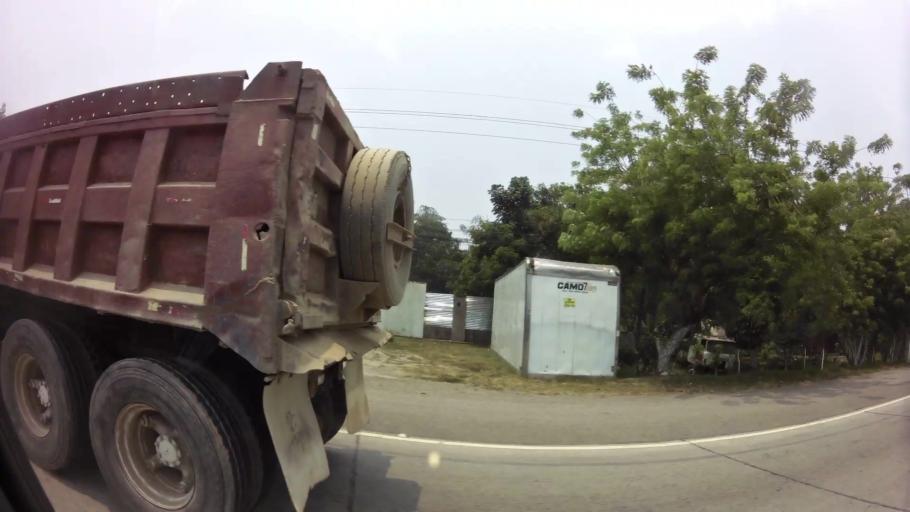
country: HN
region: Yoro
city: El Progreso
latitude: 15.4099
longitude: -87.8394
